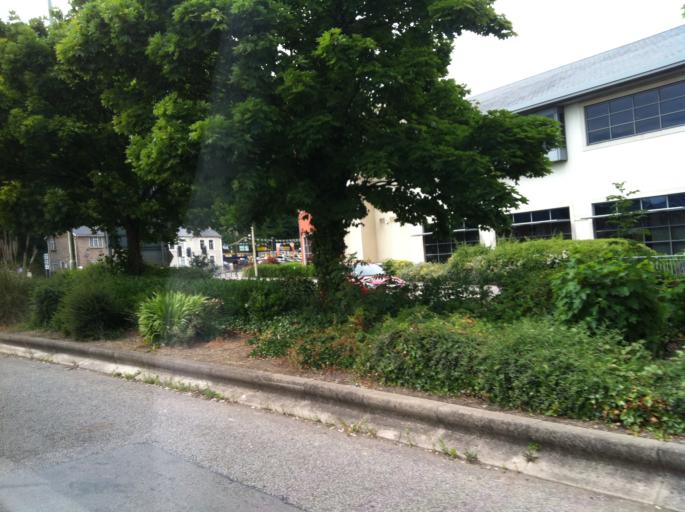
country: GB
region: Wales
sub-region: Bridgend county borough
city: Bridgend
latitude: 51.5085
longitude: -3.5806
